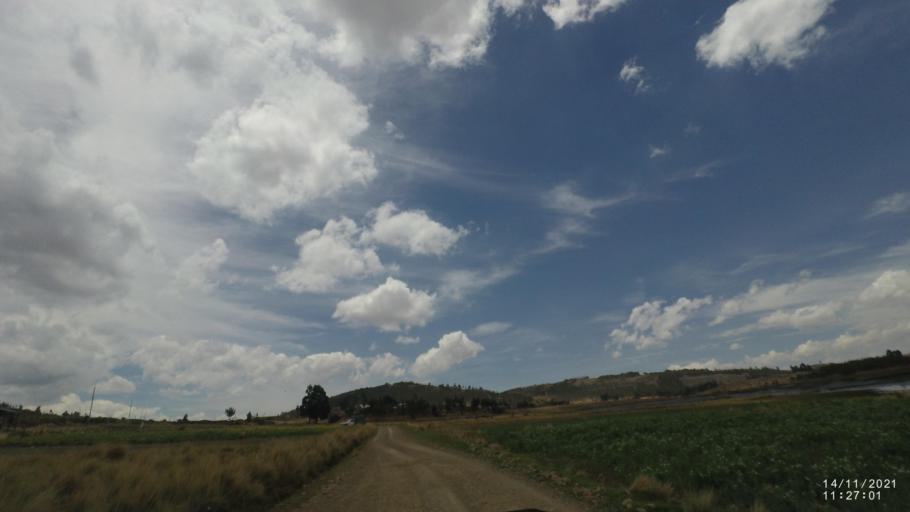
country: BO
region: Cochabamba
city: Cochabamba
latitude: -17.3390
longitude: -66.0161
